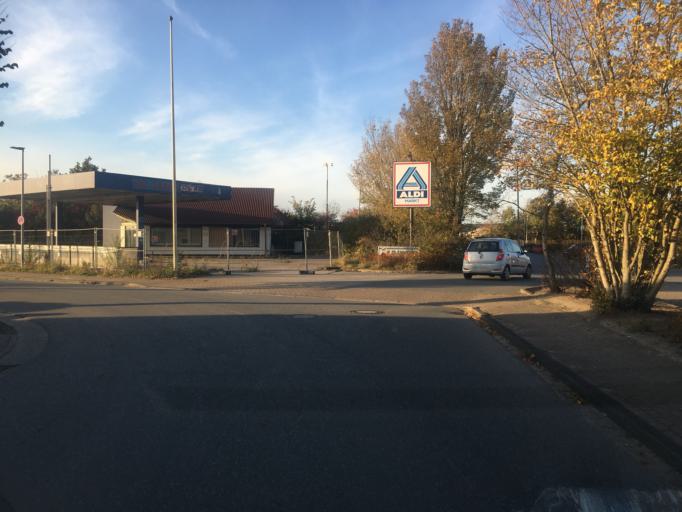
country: DE
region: Schleswig-Holstein
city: Leck
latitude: 54.7783
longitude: 8.9805
